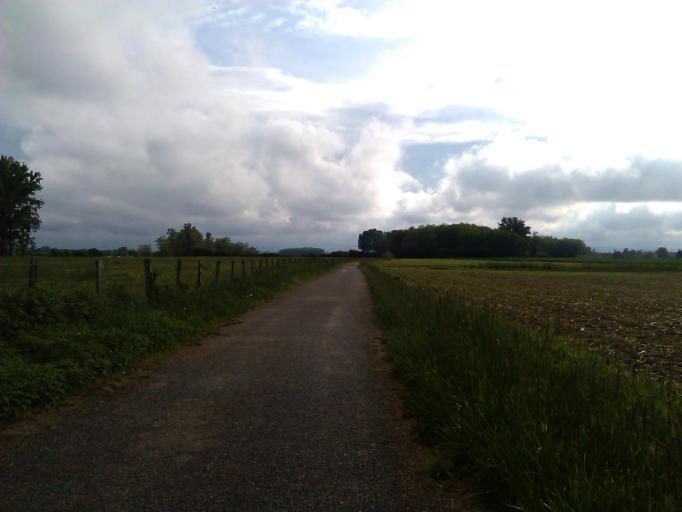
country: FR
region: Bourgogne
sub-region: Departement de Saone-et-Loire
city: Sassenay
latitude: 46.8179
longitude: 4.9067
